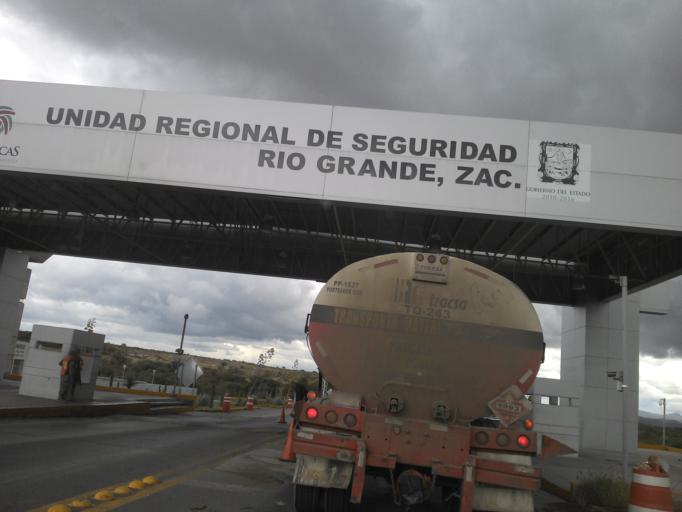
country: MX
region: Zacatecas
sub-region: Rio Grande
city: Los Condes
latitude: 23.8714
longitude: -103.0852
